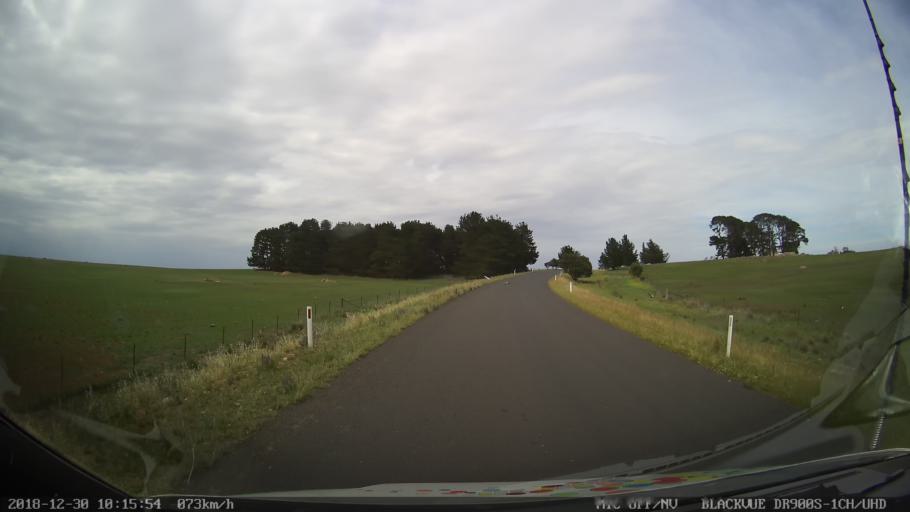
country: AU
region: New South Wales
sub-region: Snowy River
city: Berridale
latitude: -36.5462
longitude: 149.0416
